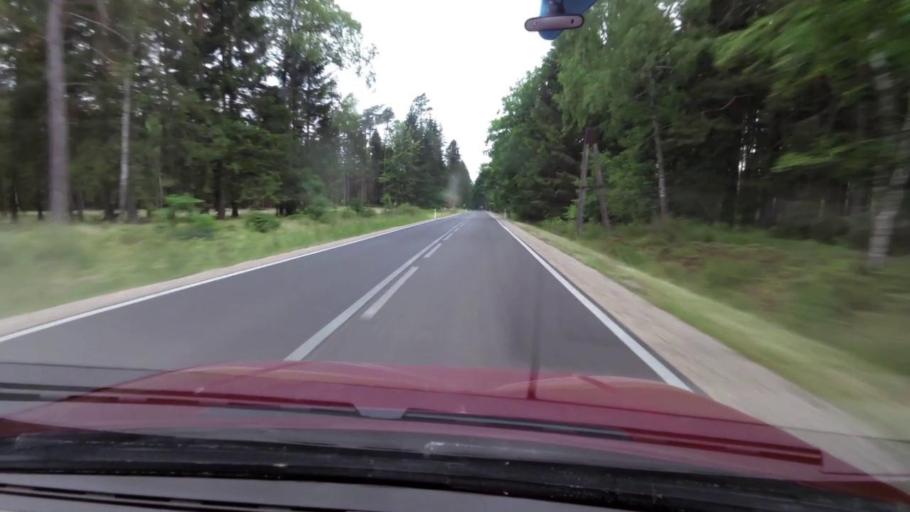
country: PL
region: West Pomeranian Voivodeship
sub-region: Powiat koszalinski
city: Sianow
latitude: 54.1511
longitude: 16.4691
